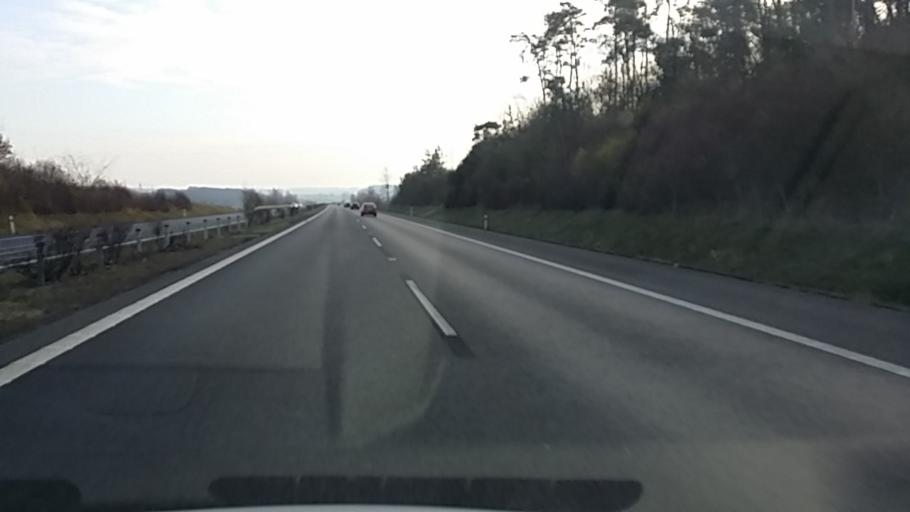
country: CZ
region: Ustecky
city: Roudnice nad Labem
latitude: 50.3891
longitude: 14.2345
